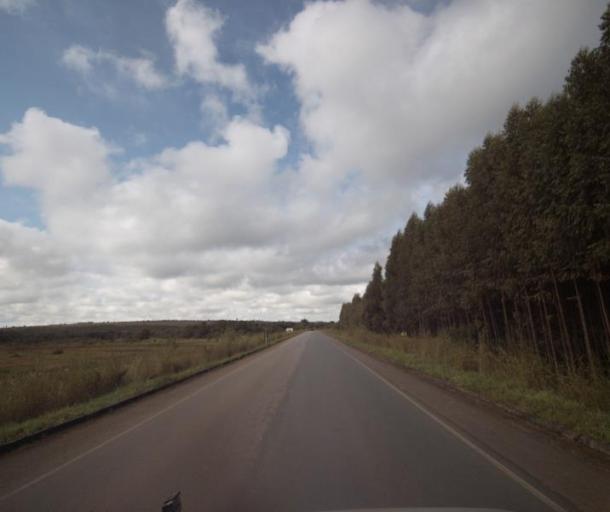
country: BR
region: Goias
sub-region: Pirenopolis
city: Pirenopolis
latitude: -15.8185
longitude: -48.7796
